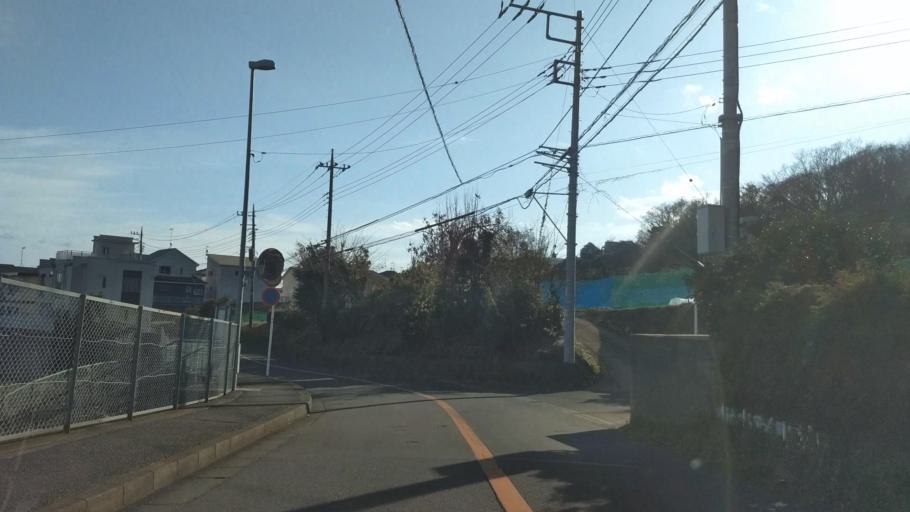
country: JP
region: Kanagawa
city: Hadano
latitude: 35.3650
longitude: 139.2517
